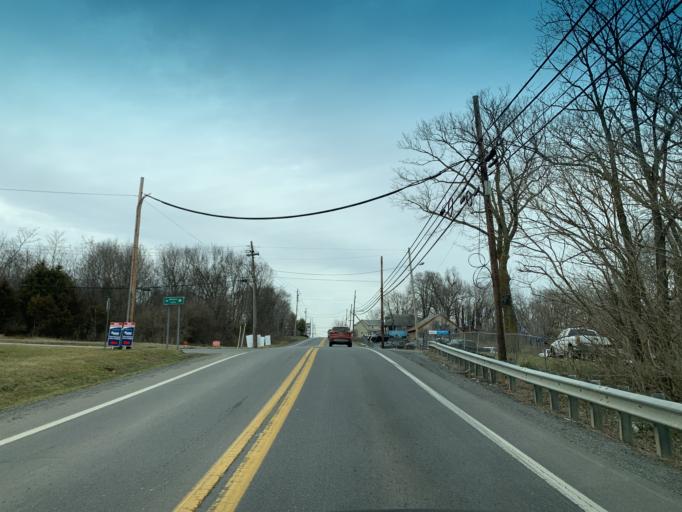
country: US
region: West Virginia
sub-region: Berkeley County
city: Martinsburg
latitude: 39.5169
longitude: -77.9279
